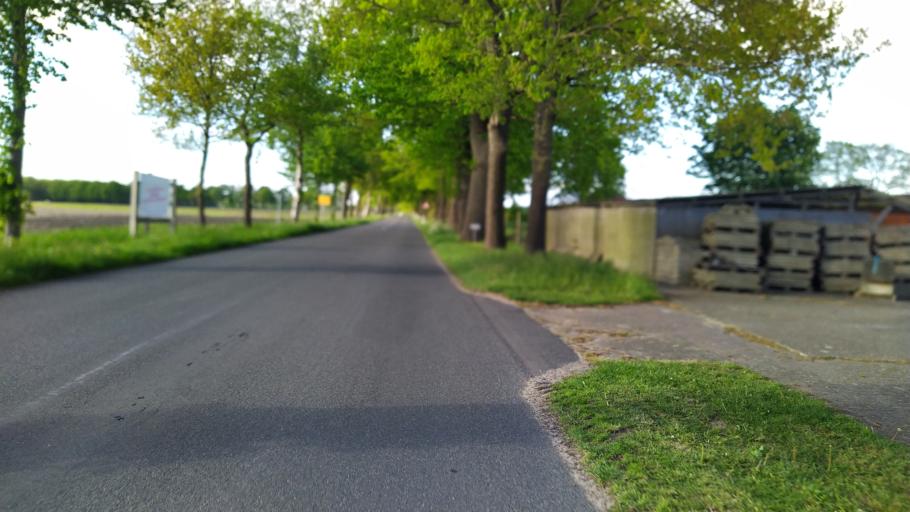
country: DE
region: Lower Saxony
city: Farven
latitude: 53.4176
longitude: 9.3333
